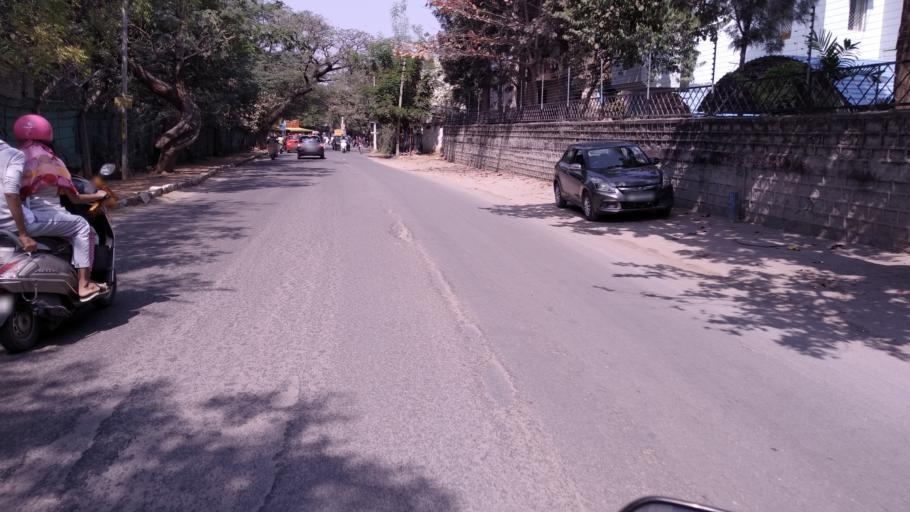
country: IN
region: Telangana
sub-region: Hyderabad
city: Malkajgiri
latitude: 17.4625
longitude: 78.4846
